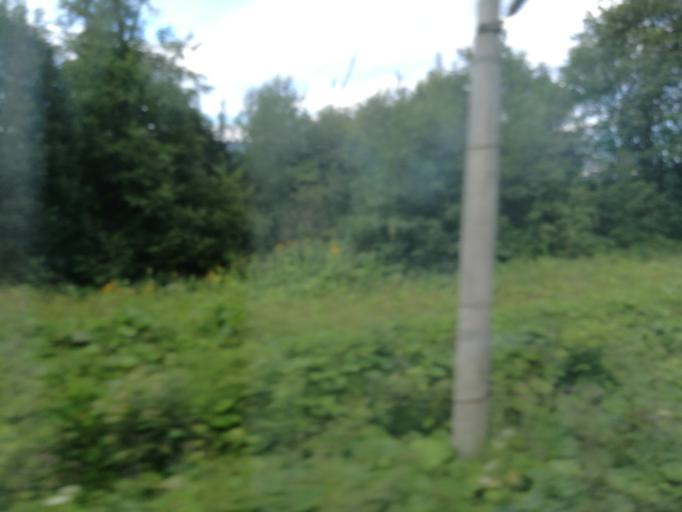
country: RO
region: Brasov
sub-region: Oras Predeal
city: Predeal
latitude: 45.5244
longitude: 25.5754
